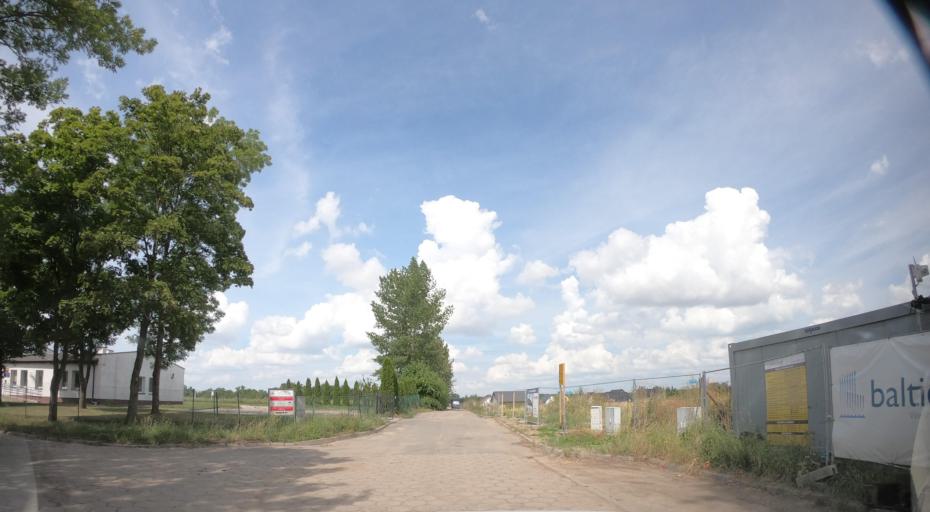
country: PL
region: West Pomeranian Voivodeship
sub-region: Powiat pyrzycki
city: Pyrzyce
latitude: 53.1308
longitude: 14.8860
